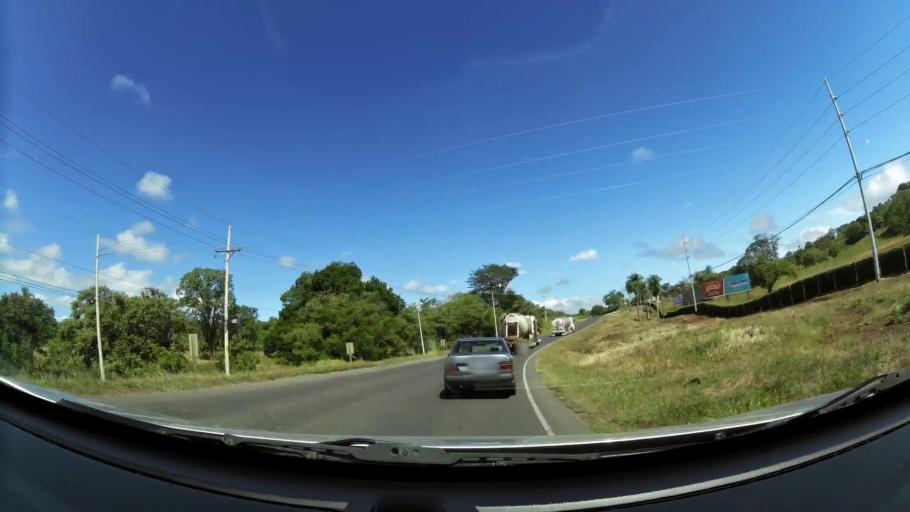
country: CR
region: Guanacaste
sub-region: Canton de Canas
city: Canas
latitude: 10.4062
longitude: -85.0863
